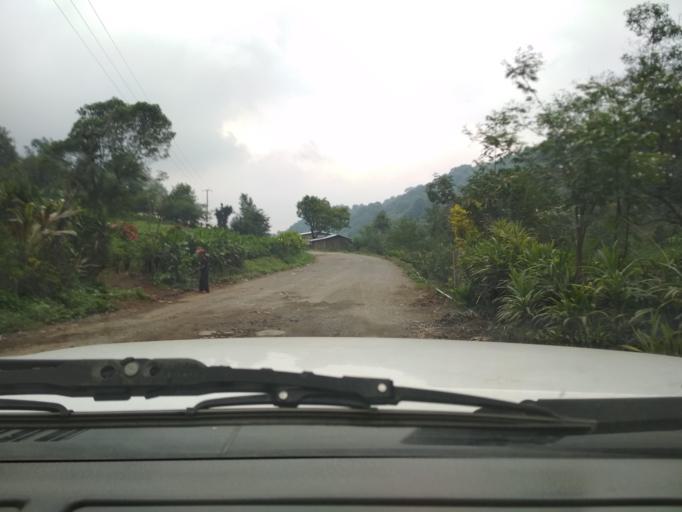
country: MX
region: Veracruz
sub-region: La Perla
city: Barrio de San Miguel
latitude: 18.9474
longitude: -97.1343
